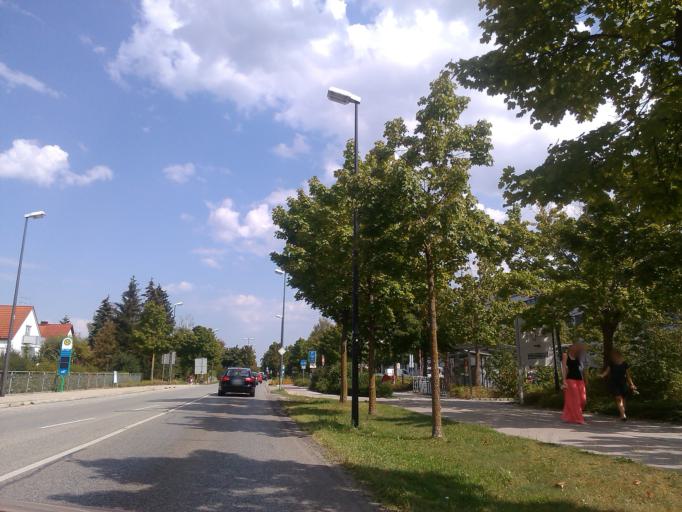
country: DE
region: Bavaria
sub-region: Upper Bavaria
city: Germering
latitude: 48.1310
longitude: 11.3657
